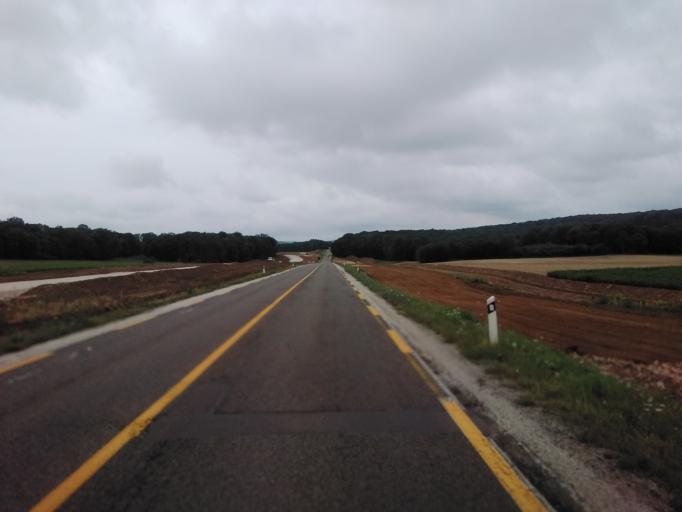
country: FR
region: Franche-Comte
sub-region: Departement de la Haute-Saone
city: Echenoz-la-Meline
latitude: 47.5192
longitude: 6.1256
